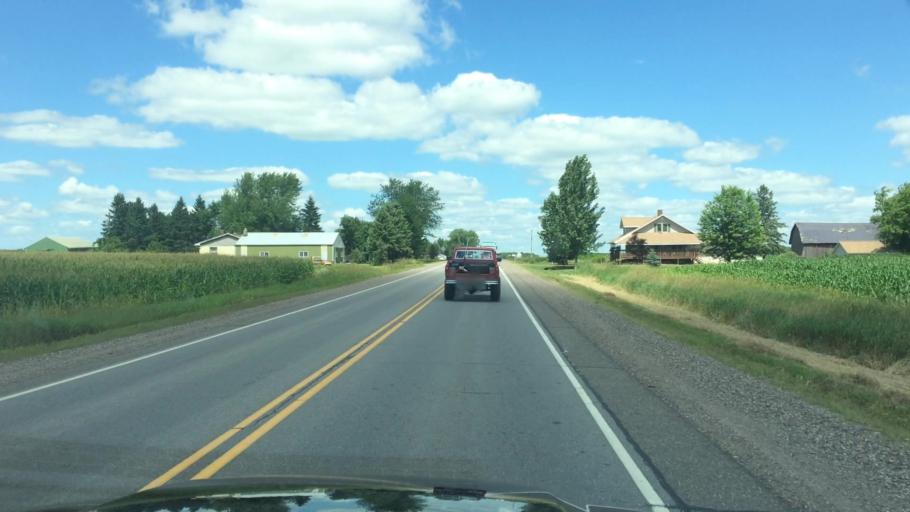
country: US
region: Wisconsin
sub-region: Taylor County
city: Medford
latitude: 45.0818
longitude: -90.3147
